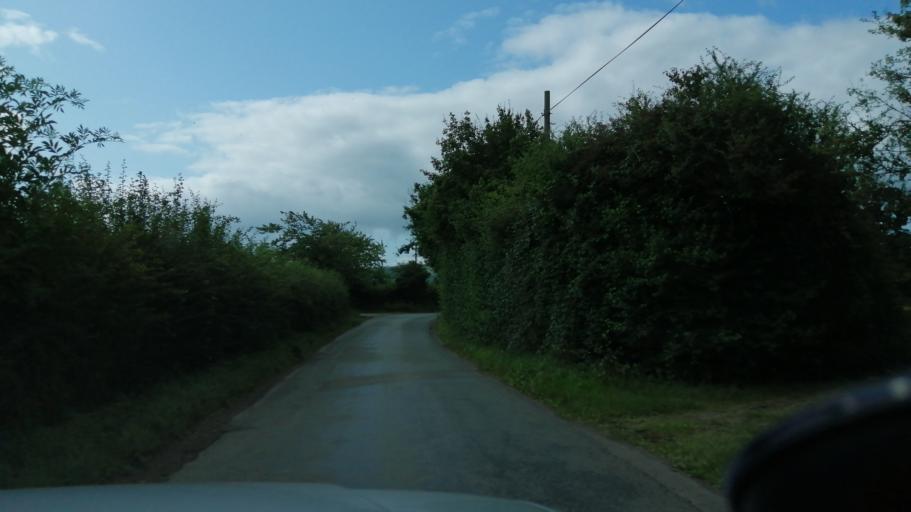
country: GB
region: England
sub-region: Herefordshire
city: Kinnersley
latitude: 52.1209
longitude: -2.9650
